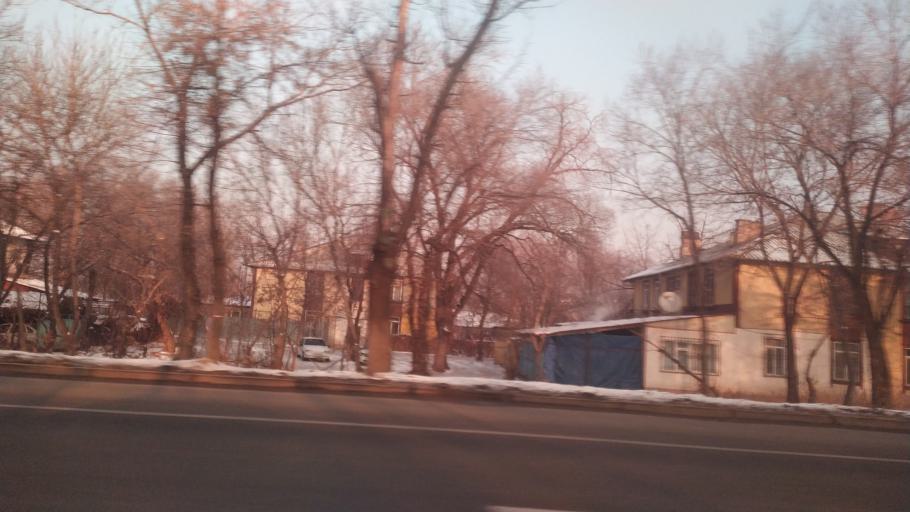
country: KZ
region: Almaty Qalasy
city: Almaty
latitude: 43.2617
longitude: 76.8937
